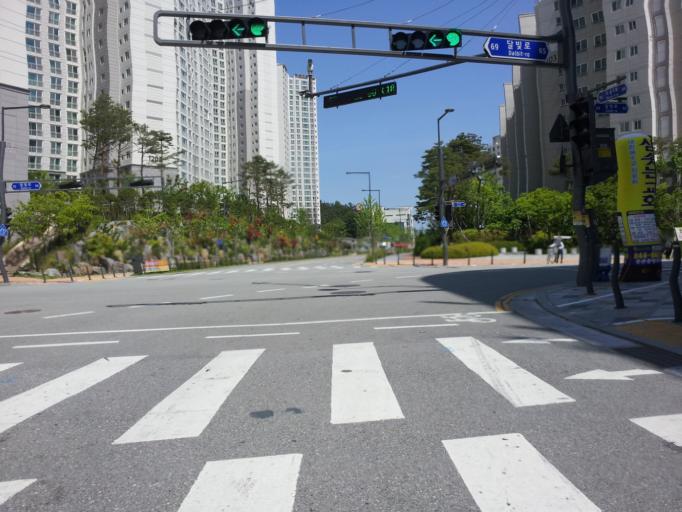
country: KR
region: Chungcheongnam-do
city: Gongju
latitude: 36.5051
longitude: 127.2496
